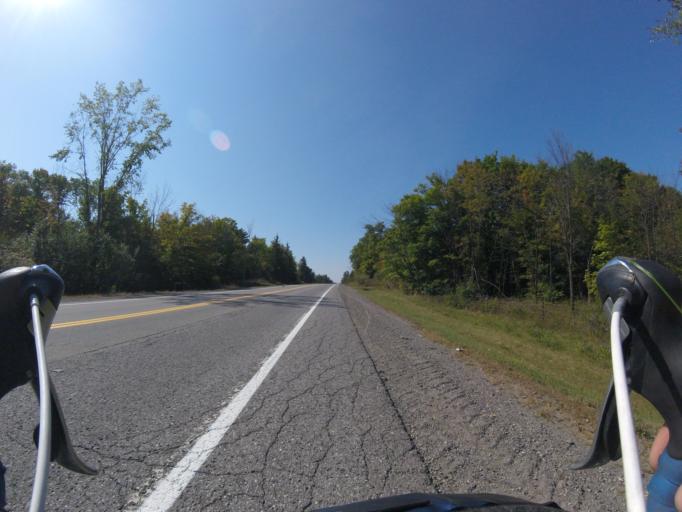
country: CA
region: Ontario
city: Bells Corners
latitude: 45.3181
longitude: -75.8586
